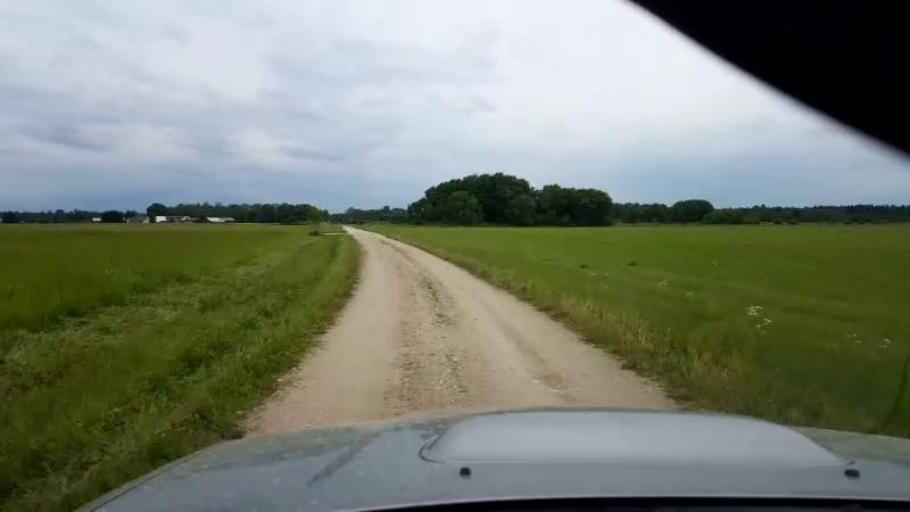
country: EE
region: Paernumaa
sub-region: Tootsi vald
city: Tootsi
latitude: 58.5897
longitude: 24.6581
